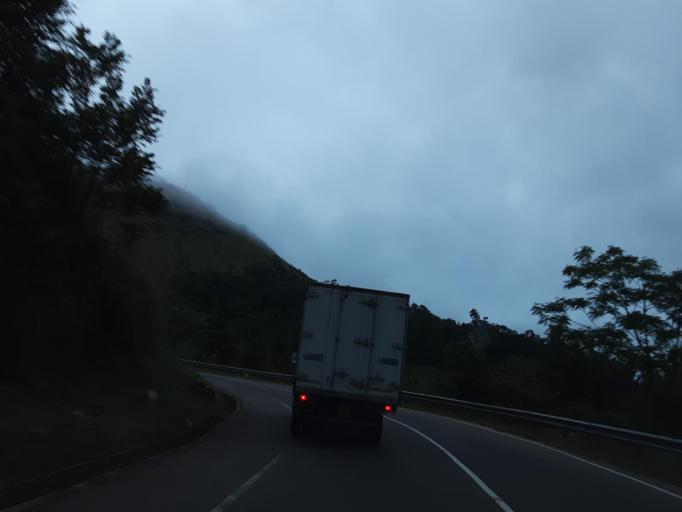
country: LK
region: Uva
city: Badulla
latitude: 6.9148
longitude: 80.9540
